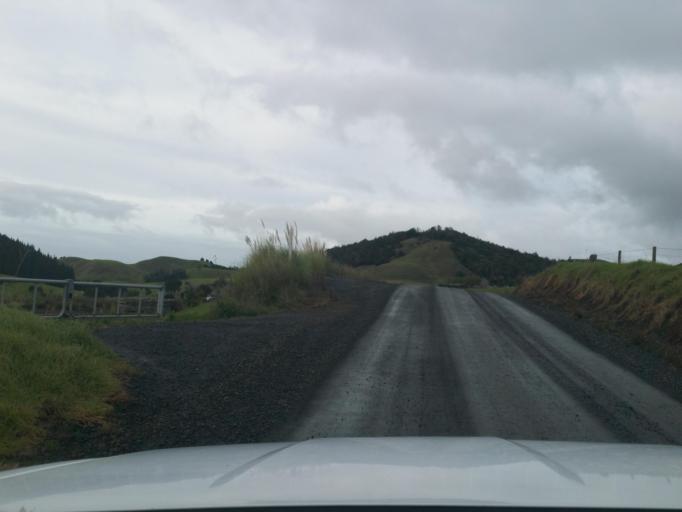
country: NZ
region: Northland
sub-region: Kaipara District
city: Dargaville
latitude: -35.8210
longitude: 173.8156
